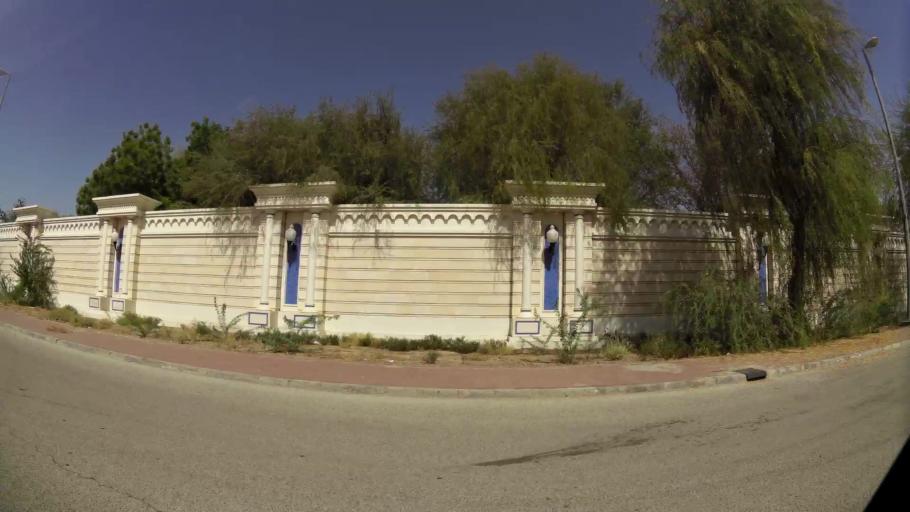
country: OM
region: Al Buraimi
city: Al Buraymi
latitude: 24.2906
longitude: 55.7743
